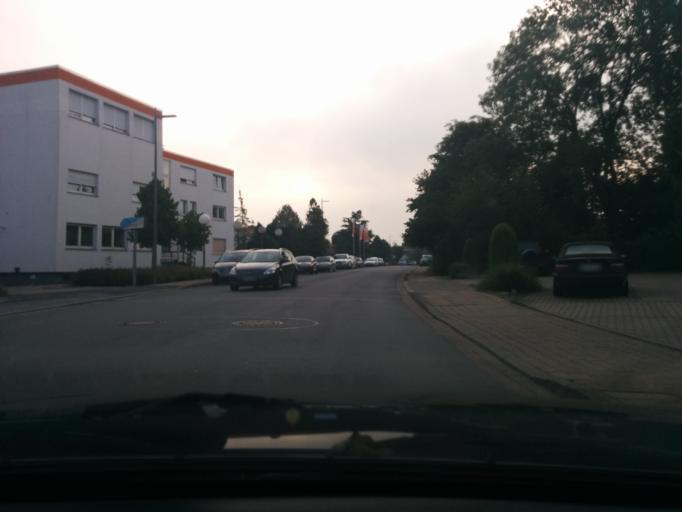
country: DE
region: North Rhine-Westphalia
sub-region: Regierungsbezirk Detmold
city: Bielefeld
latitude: 52.0067
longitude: 8.5851
